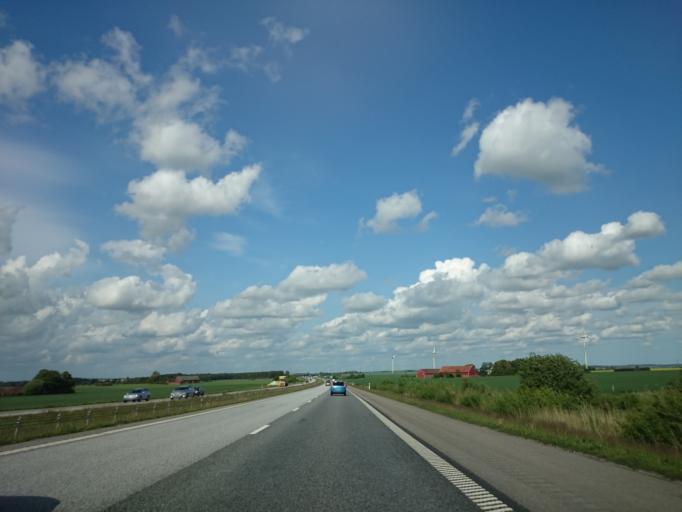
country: SE
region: Skane
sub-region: Eslovs Kommun
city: Eslov
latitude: 55.7519
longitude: 13.2740
